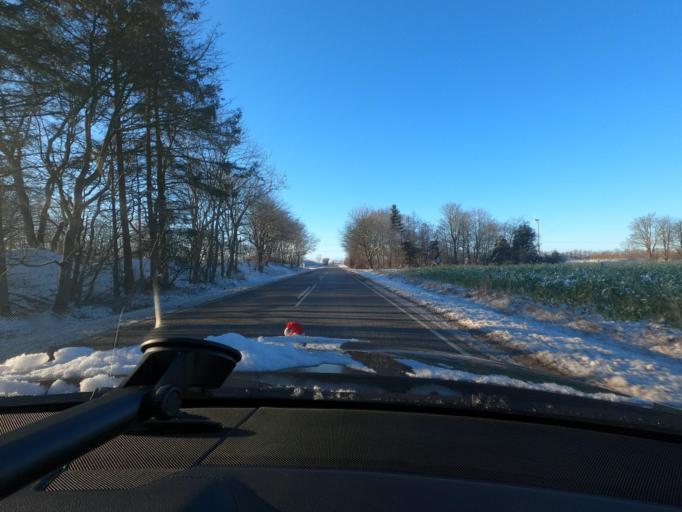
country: DK
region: South Denmark
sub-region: Aabenraa Kommune
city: Rodekro
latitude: 55.0746
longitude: 9.2733
